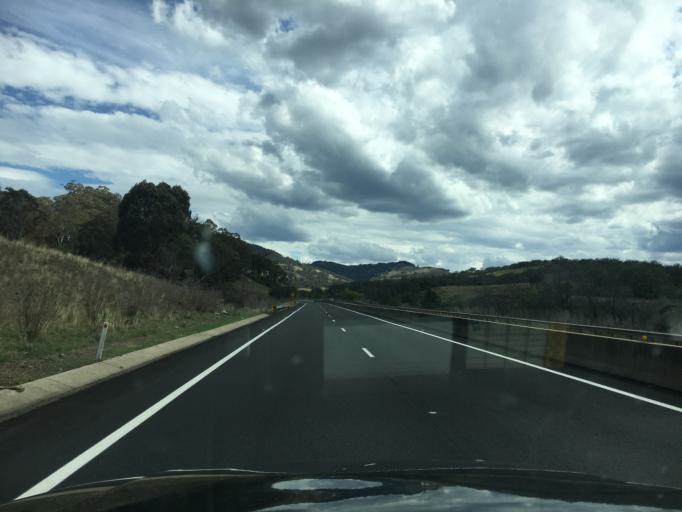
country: AU
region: New South Wales
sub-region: Liverpool Plains
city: Quirindi
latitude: -31.7270
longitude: 150.7850
